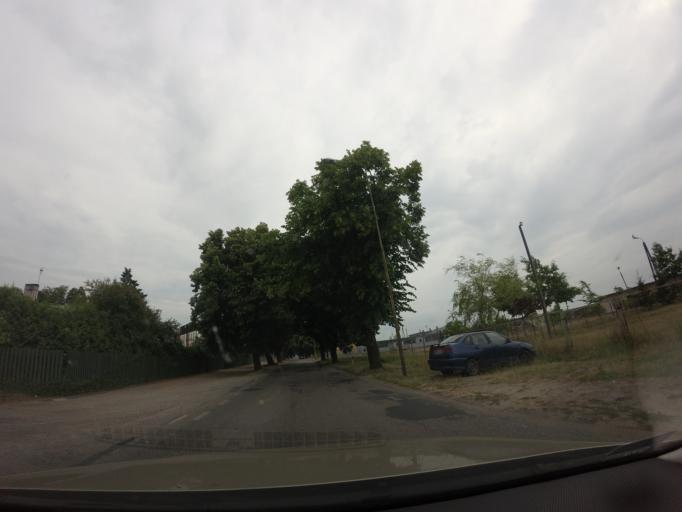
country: PL
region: West Pomeranian Voivodeship
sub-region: Powiat drawski
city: Czaplinek
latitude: 53.5490
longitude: 16.2323
